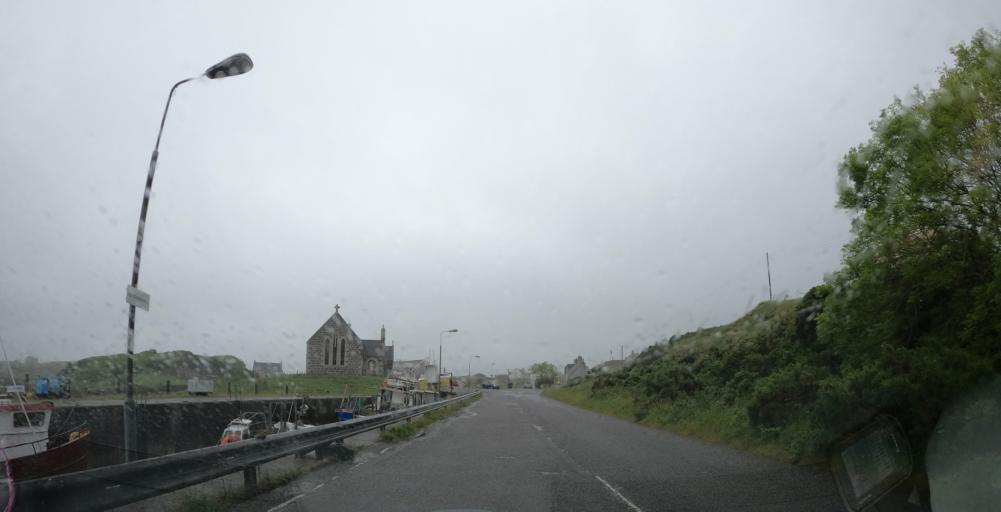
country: GB
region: Scotland
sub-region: Eilean Siar
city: Barra
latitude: 57.0011
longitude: -7.4268
